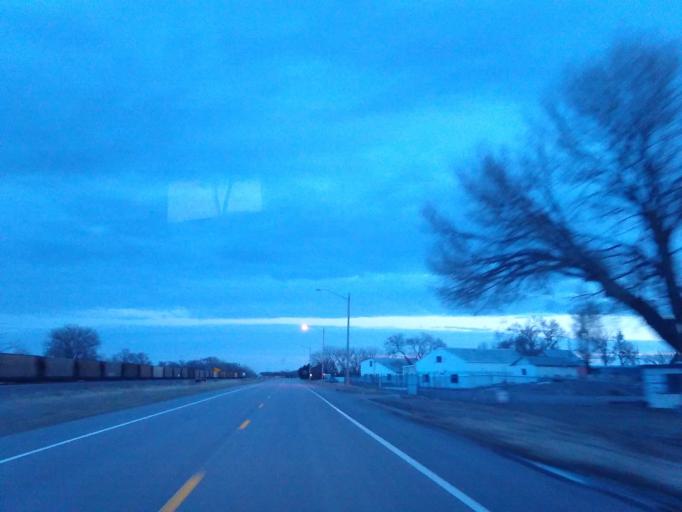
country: US
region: Nebraska
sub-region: Garden County
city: Oshkosh
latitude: 41.3302
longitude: -102.1383
